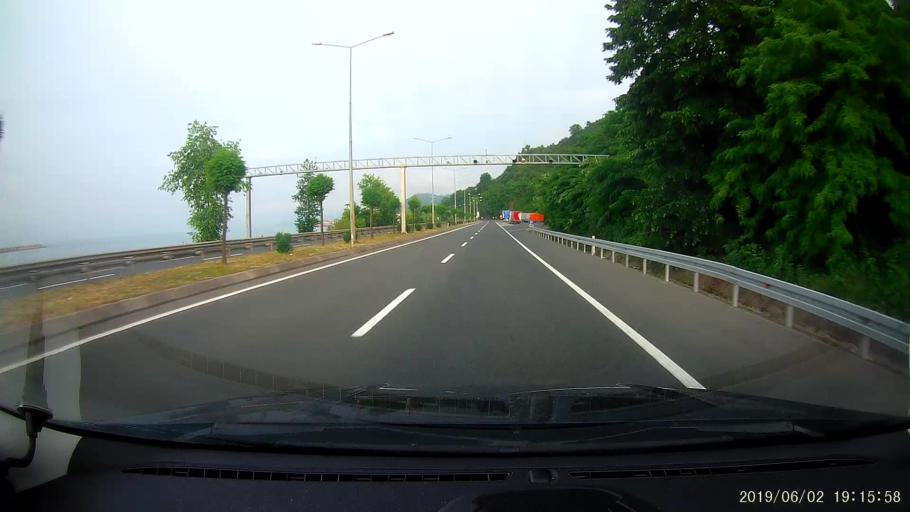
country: TR
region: Giresun
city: Piraziz
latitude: 40.9598
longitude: 38.1064
